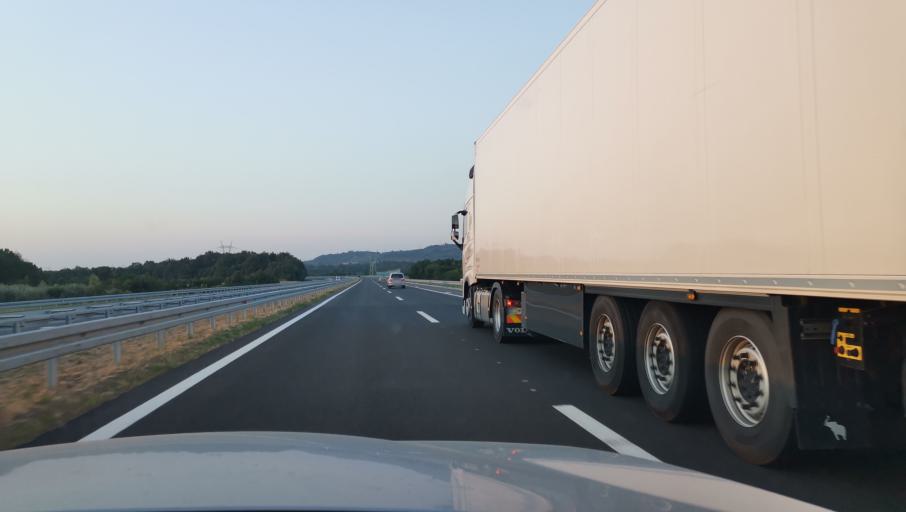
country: RS
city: Zvecka
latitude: 44.5905
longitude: 20.1984
